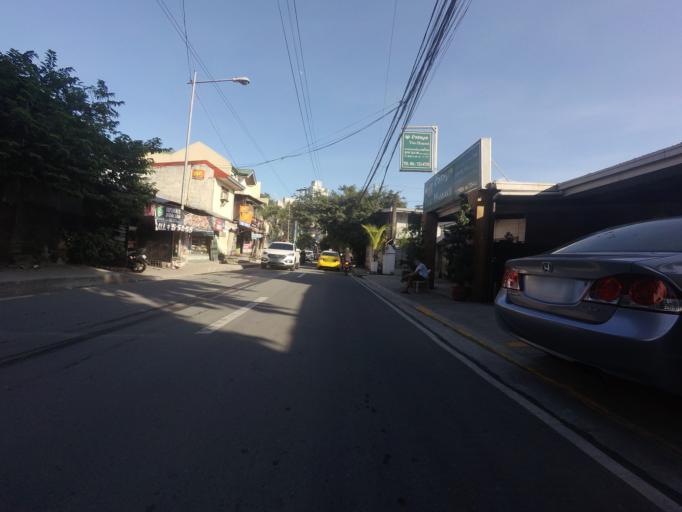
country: PH
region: Metro Manila
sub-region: San Juan
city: San Juan
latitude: 14.5914
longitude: 121.0352
